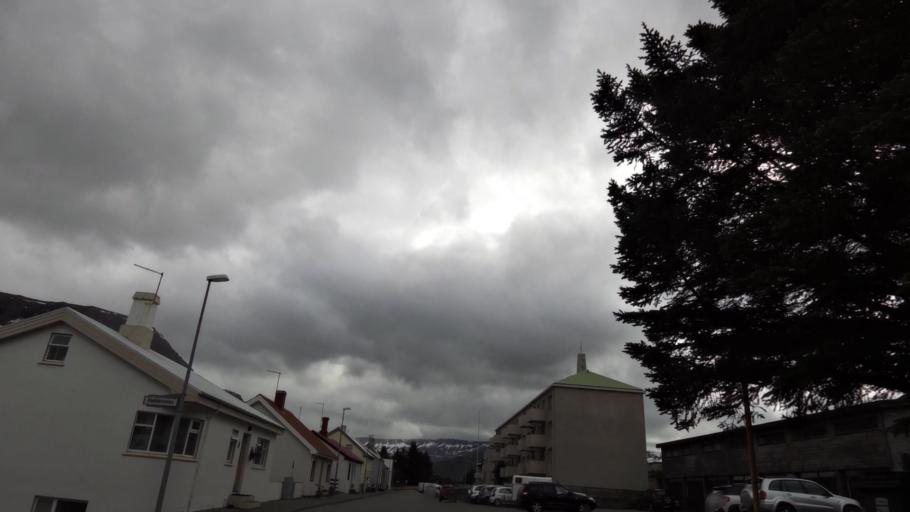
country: IS
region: Westfjords
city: Isafjoerdur
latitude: 66.0772
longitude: -23.1283
